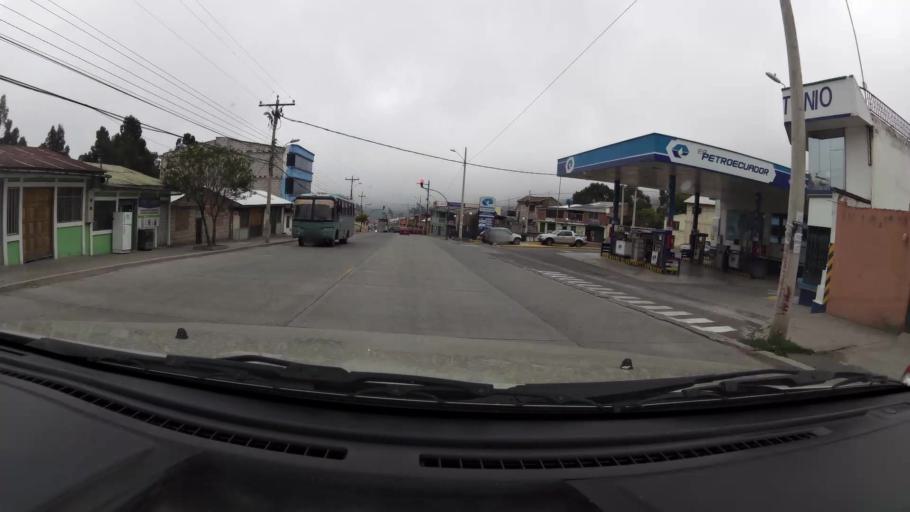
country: EC
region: Canar
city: Canar
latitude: -2.5511
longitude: -78.9411
